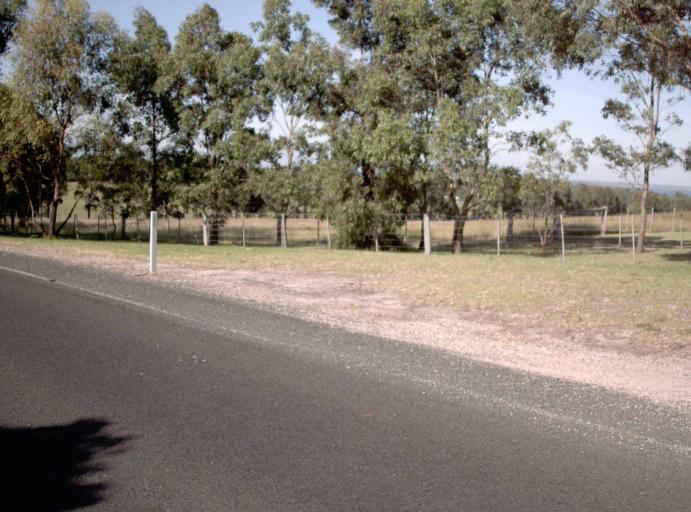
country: AU
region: Victoria
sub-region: East Gippsland
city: Lakes Entrance
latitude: -37.8701
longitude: 147.8476
